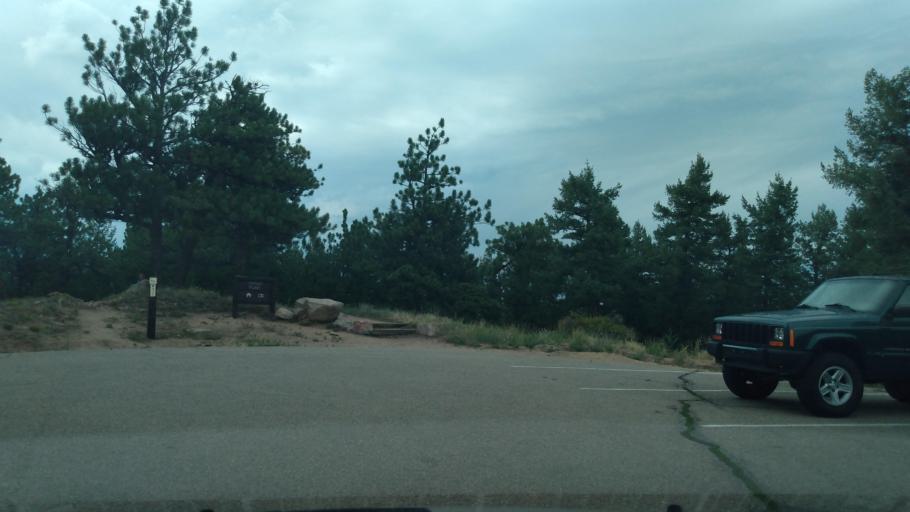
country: US
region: Colorado
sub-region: Boulder County
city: Boulder
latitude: 40.0050
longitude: -105.3064
